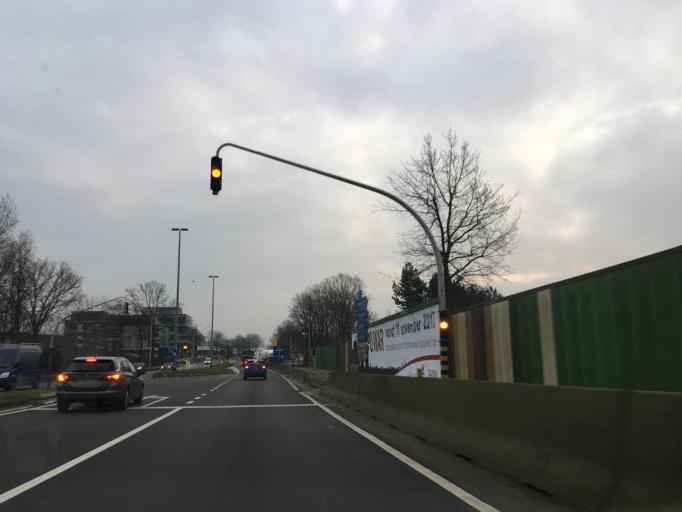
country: BE
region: Flanders
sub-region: Provincie West-Vlaanderen
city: Waregem
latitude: 50.8770
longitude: 3.4285
